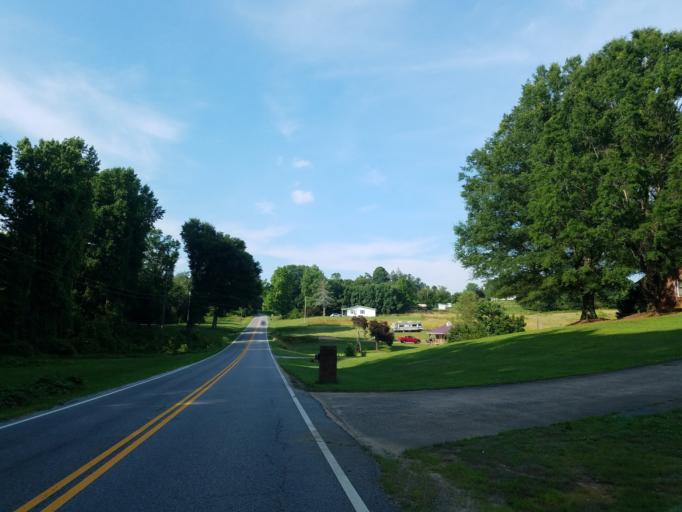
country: US
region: Georgia
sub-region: Forsyth County
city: Cumming
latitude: 34.2872
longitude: -84.0686
